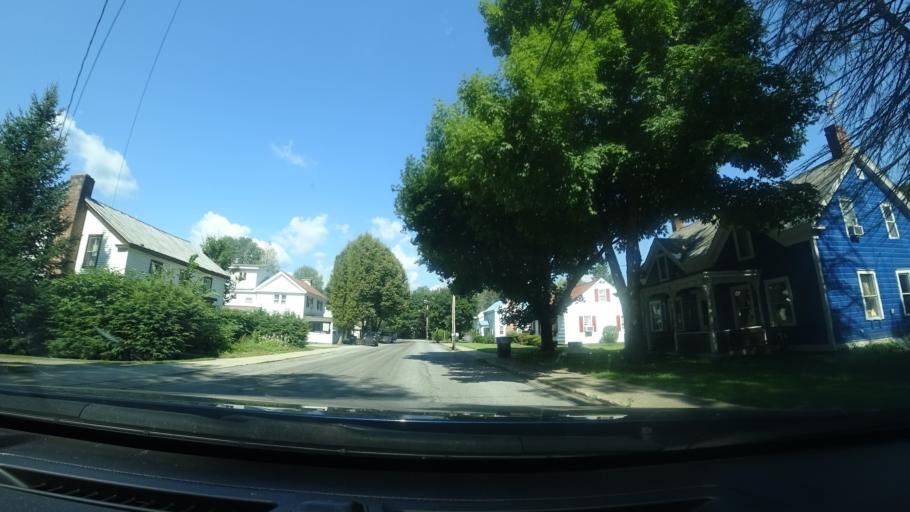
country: US
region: New York
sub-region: Warren County
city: Warrensburg
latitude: 43.6537
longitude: -73.8038
